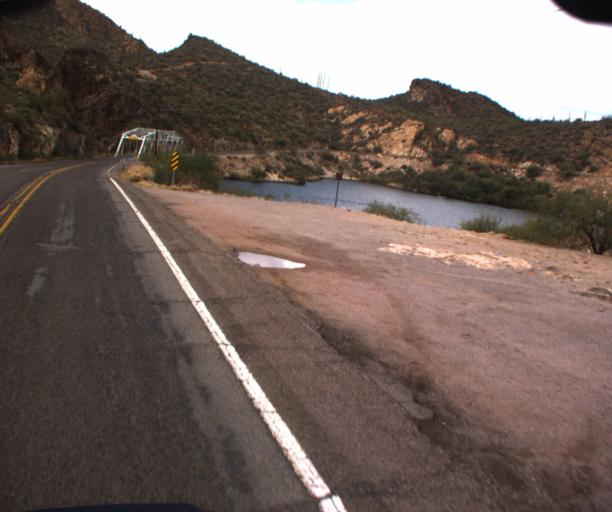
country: US
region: Arizona
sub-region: Pinal County
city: Apache Junction
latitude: 33.5385
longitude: -111.4416
